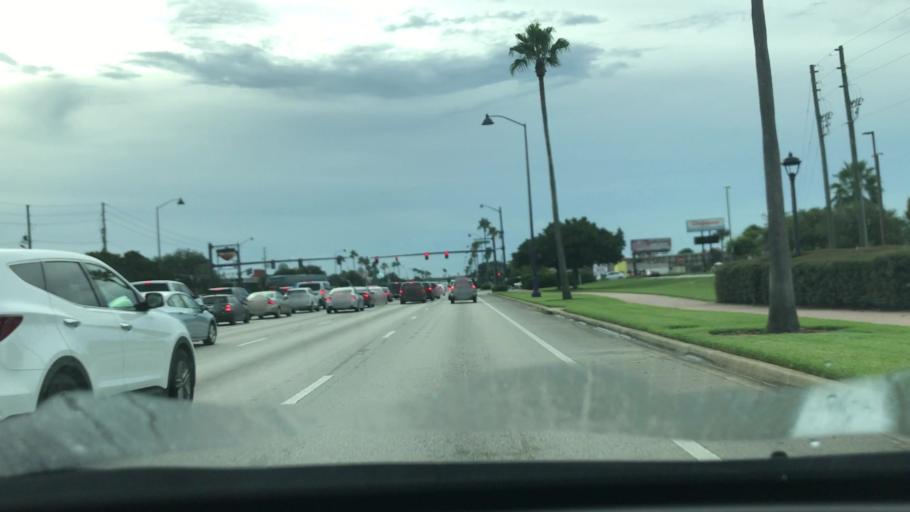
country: US
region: Florida
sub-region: Polk County
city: Citrus Ridge
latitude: 28.3393
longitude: -81.5958
